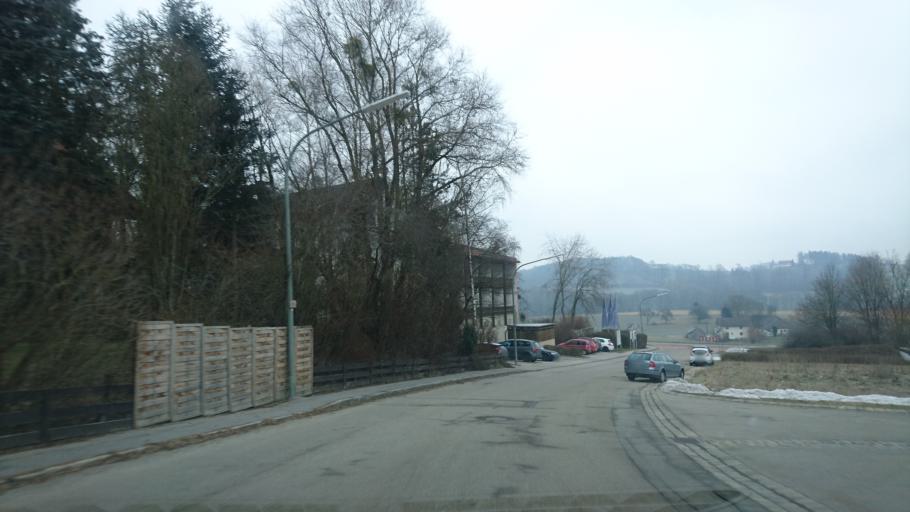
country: DE
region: Bavaria
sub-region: Lower Bavaria
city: Bad Griesbach
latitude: 48.4396
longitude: 13.1962
